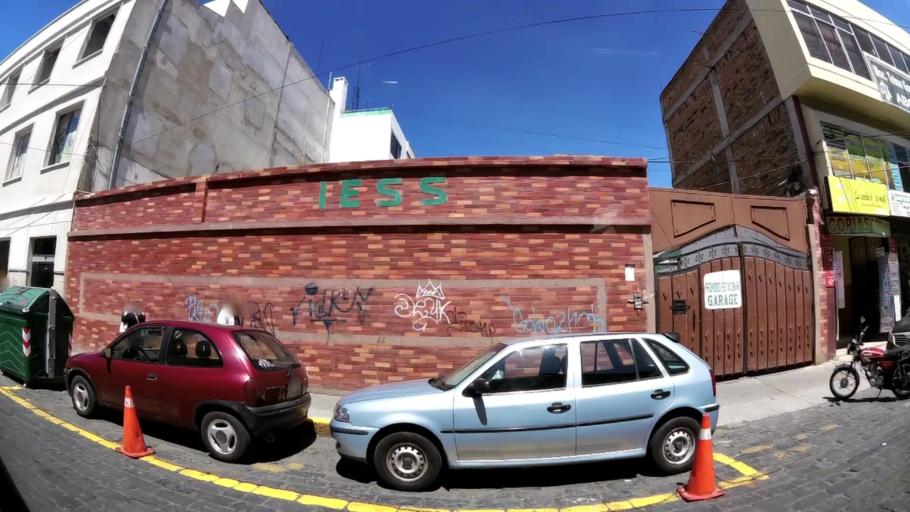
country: EC
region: Chimborazo
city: Riobamba
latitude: -1.6706
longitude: -78.6519
